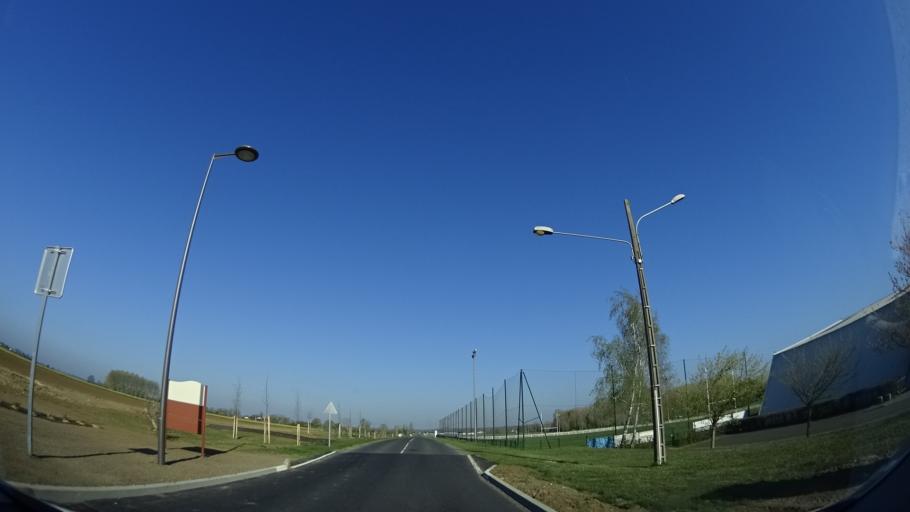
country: FR
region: Pays de la Loire
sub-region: Departement de Maine-et-Loire
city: Doue-la-Fontaine
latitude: 47.2017
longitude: -0.2835
